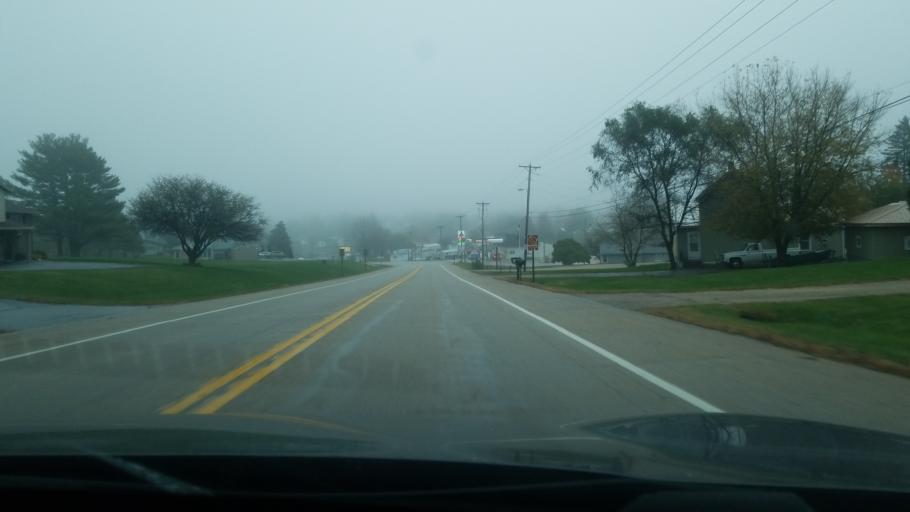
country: US
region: Wisconsin
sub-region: Lafayette County
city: Shullsburg
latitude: 42.5728
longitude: -90.2414
